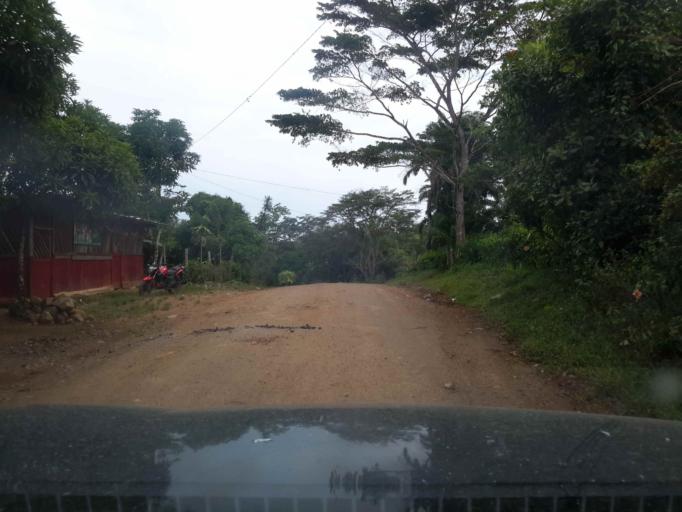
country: CR
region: Alajuela
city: Los Chiles
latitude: 11.0853
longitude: -84.5098
